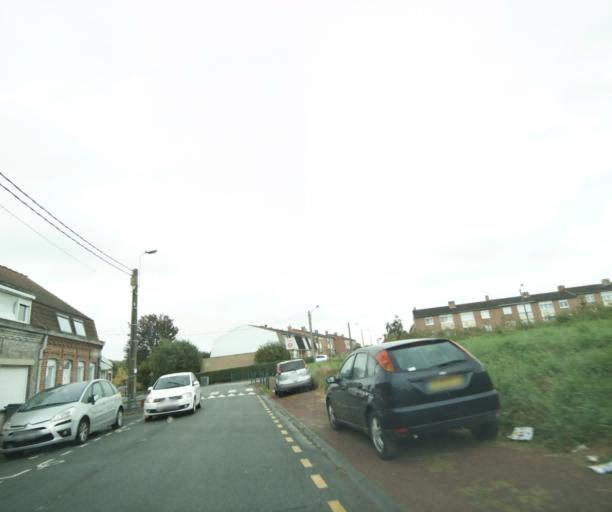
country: FR
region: Nord-Pas-de-Calais
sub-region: Departement du Nord
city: Roncq
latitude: 50.7442
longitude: 3.1284
